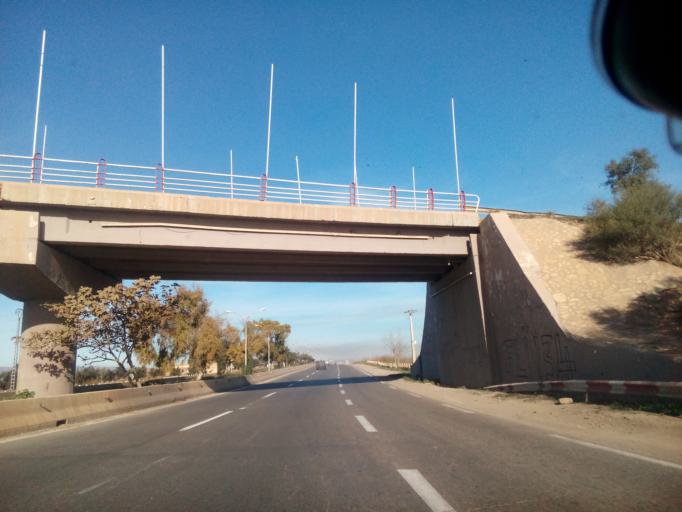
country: DZ
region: Oran
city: Ain el Bya
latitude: 35.7854
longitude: -0.2850
